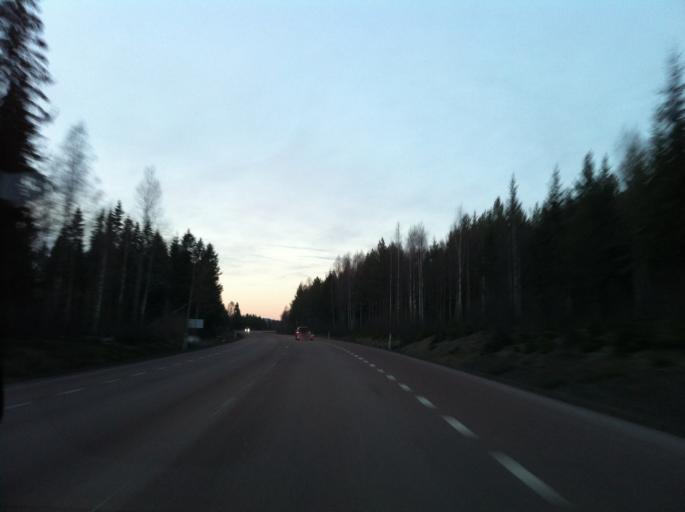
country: SE
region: Dalarna
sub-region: Orsa Kommun
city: Orsa
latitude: 61.0514
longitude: 14.6103
